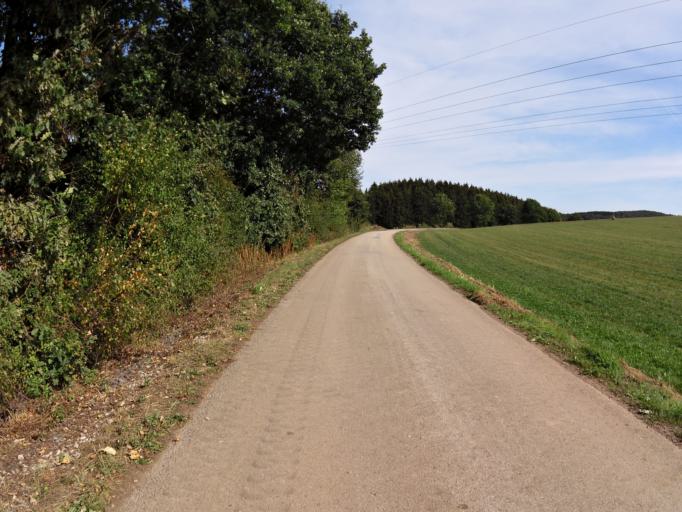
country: DE
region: Rheinland-Pfalz
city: Euscheid
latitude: 50.1274
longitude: 6.2842
